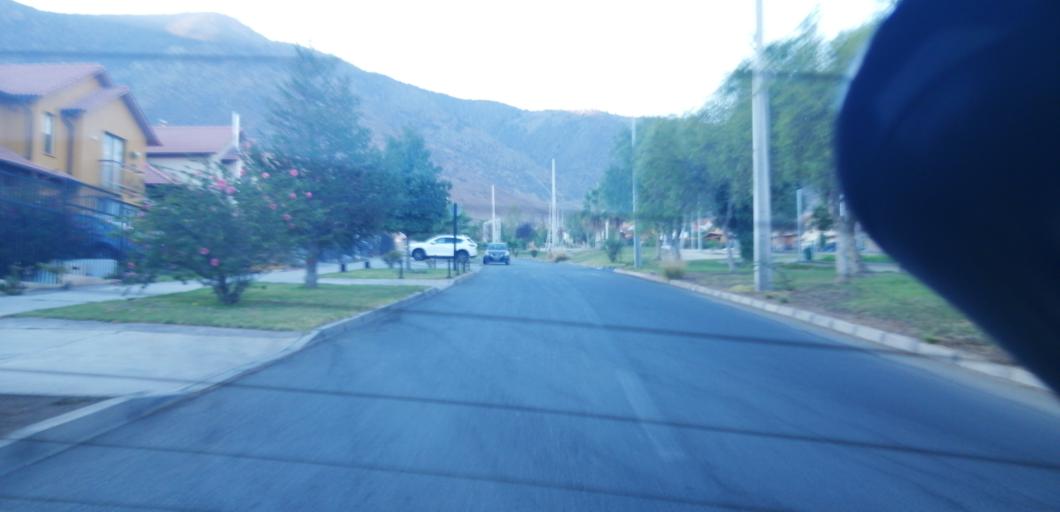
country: CL
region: Santiago Metropolitan
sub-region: Provincia de Santiago
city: Lo Prado
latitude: -33.4574
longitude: -70.8446
